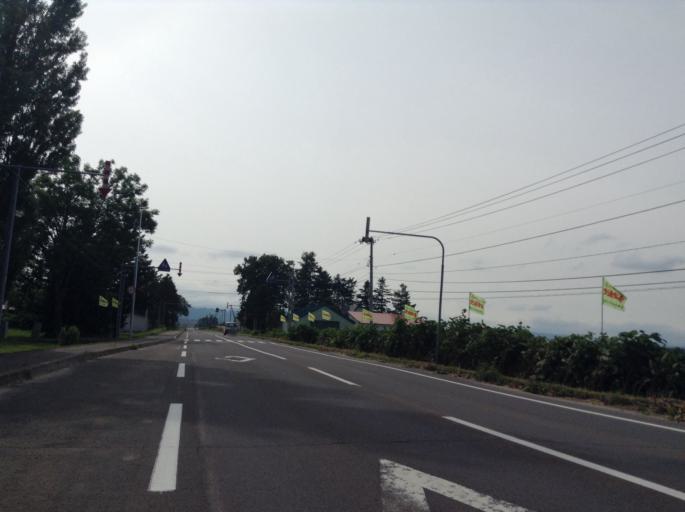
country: JP
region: Hokkaido
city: Nayoro
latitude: 44.4386
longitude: 142.3966
